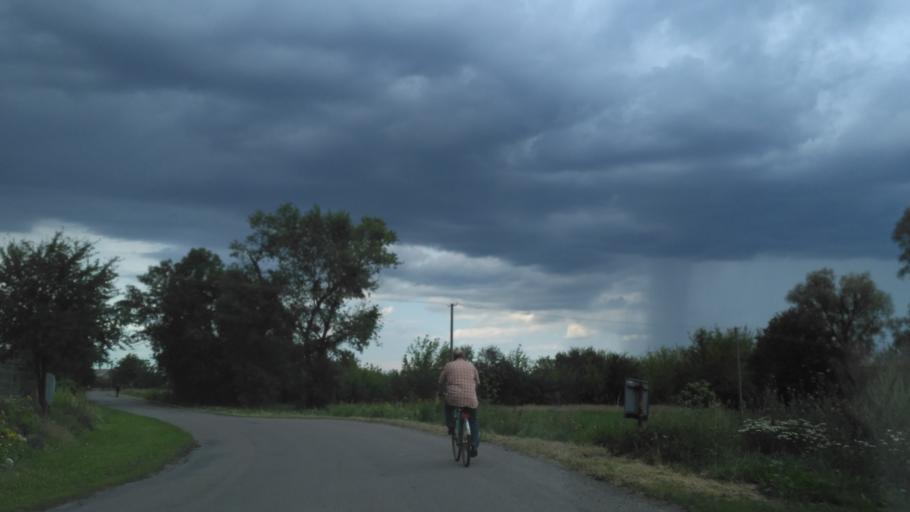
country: PL
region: Lublin Voivodeship
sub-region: Powiat leczynski
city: Milejow
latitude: 51.2143
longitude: 22.8892
